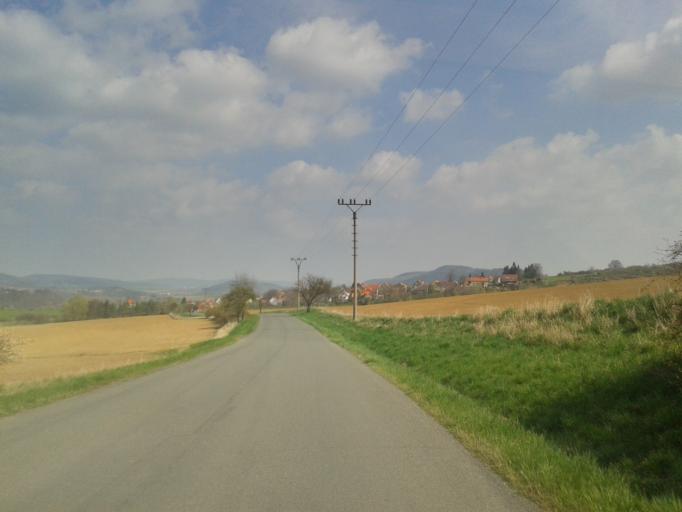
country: CZ
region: Central Bohemia
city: Lochovice
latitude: 49.8756
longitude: 13.9507
